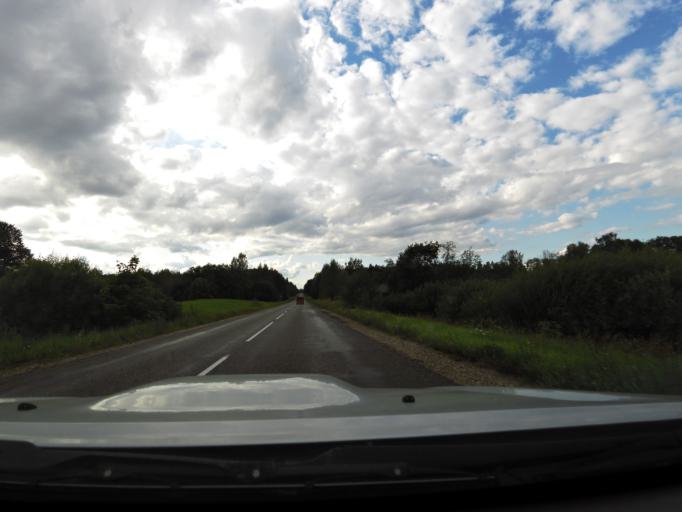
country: LV
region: Akniste
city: Akniste
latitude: 56.0032
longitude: 25.9510
